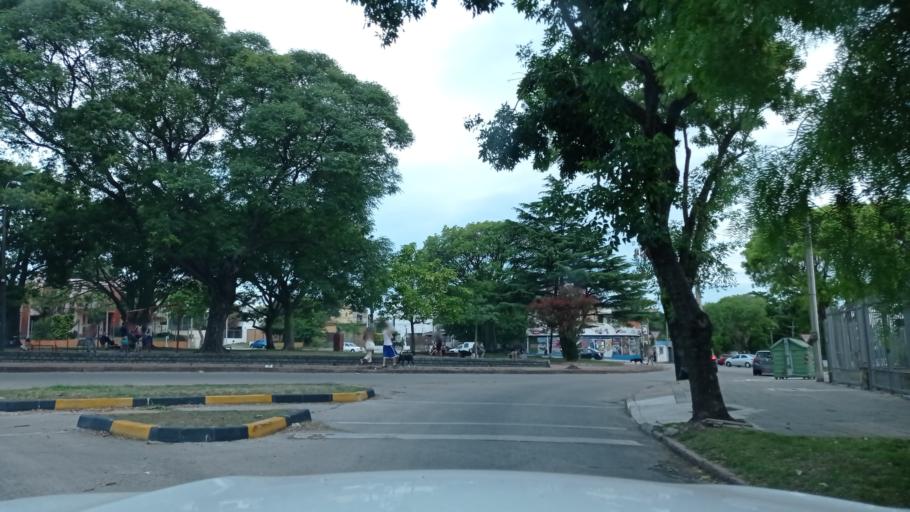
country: UY
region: Canelones
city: Paso de Carrasco
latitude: -34.8918
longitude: -56.1170
